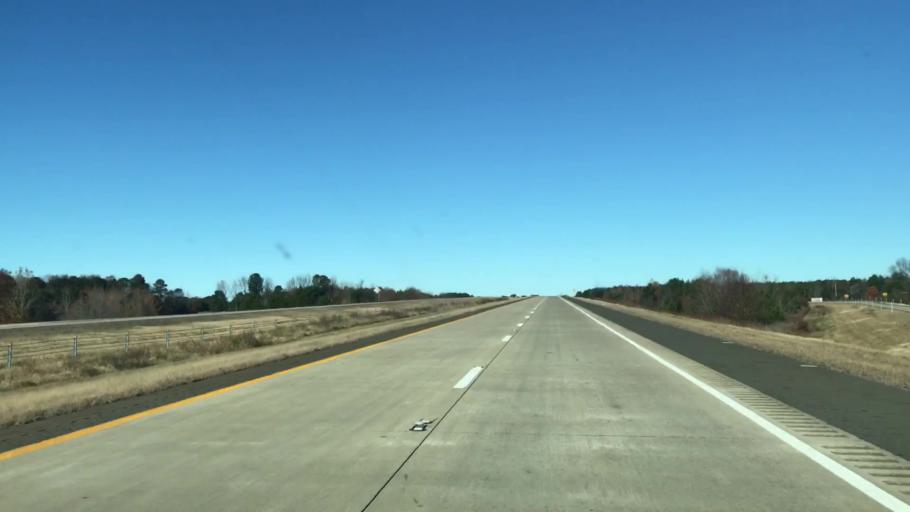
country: US
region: Texas
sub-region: Bowie County
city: Texarkana
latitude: 33.2475
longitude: -93.8816
